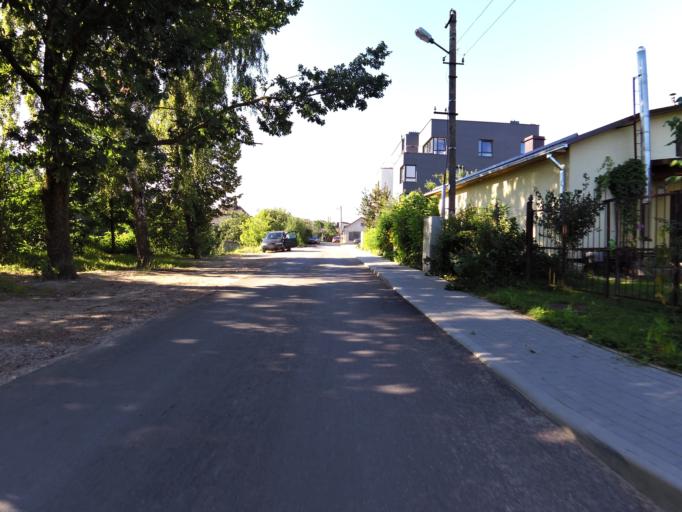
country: LT
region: Vilnius County
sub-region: Vilnius
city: Vilnius
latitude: 54.7094
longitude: 25.2767
